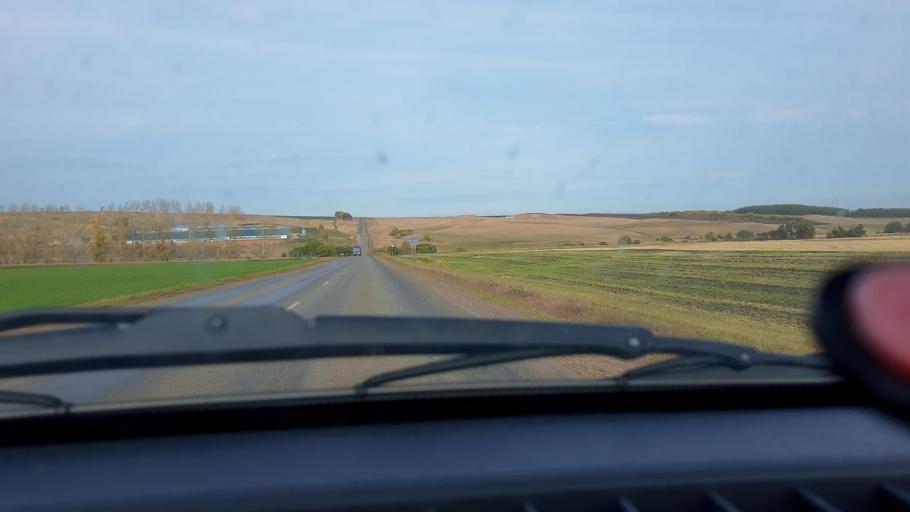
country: RU
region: Bashkortostan
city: Chekmagush
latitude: 55.0567
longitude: 54.6239
